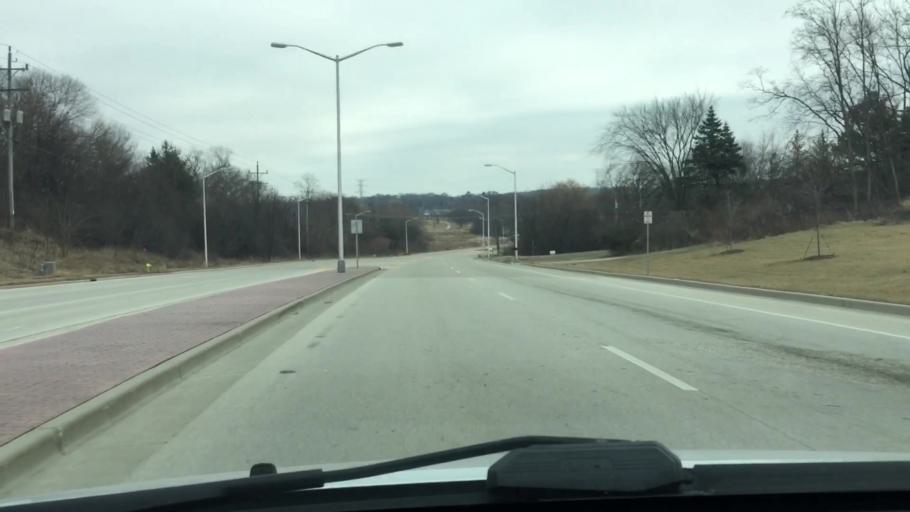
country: US
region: Wisconsin
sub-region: Waukesha County
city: Waukesha
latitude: 42.9886
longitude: -88.2178
